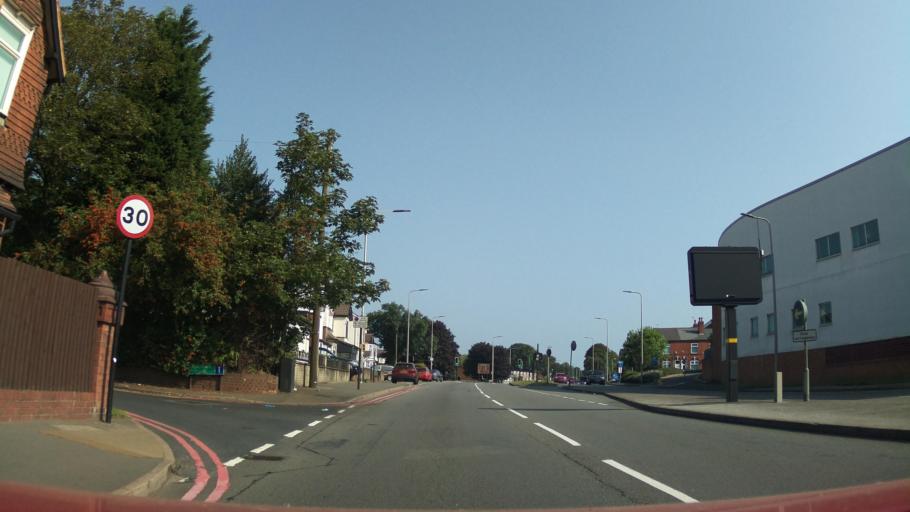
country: GB
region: England
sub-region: Sandwell
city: West Bromwich
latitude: 52.5283
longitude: -1.9904
